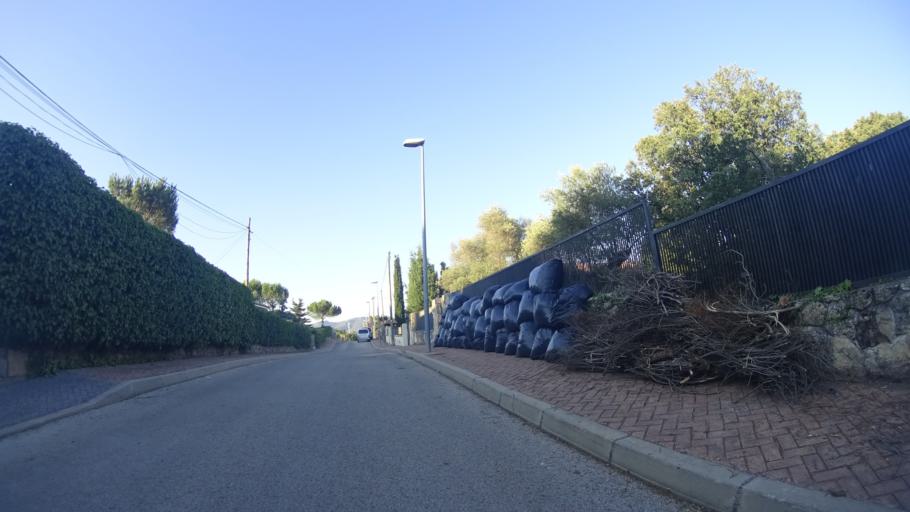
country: ES
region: Madrid
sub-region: Provincia de Madrid
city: Galapagar
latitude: 40.5689
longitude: -4.0004
